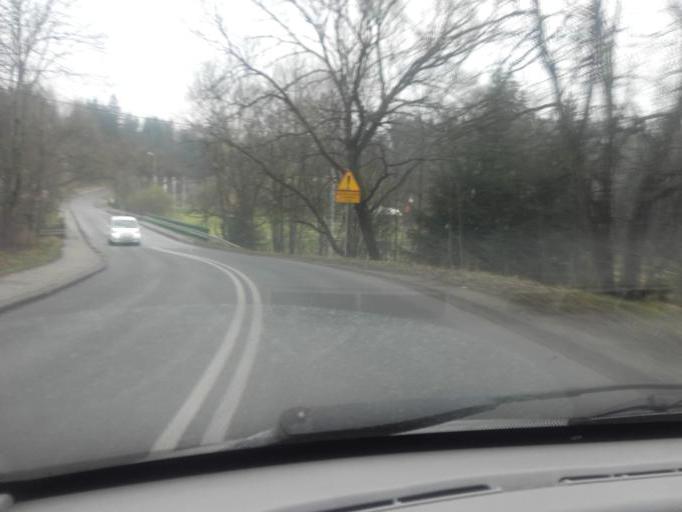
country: PL
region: Silesian Voivodeship
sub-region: Powiat cieszynski
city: Istebna
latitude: 49.5726
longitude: 18.8929
